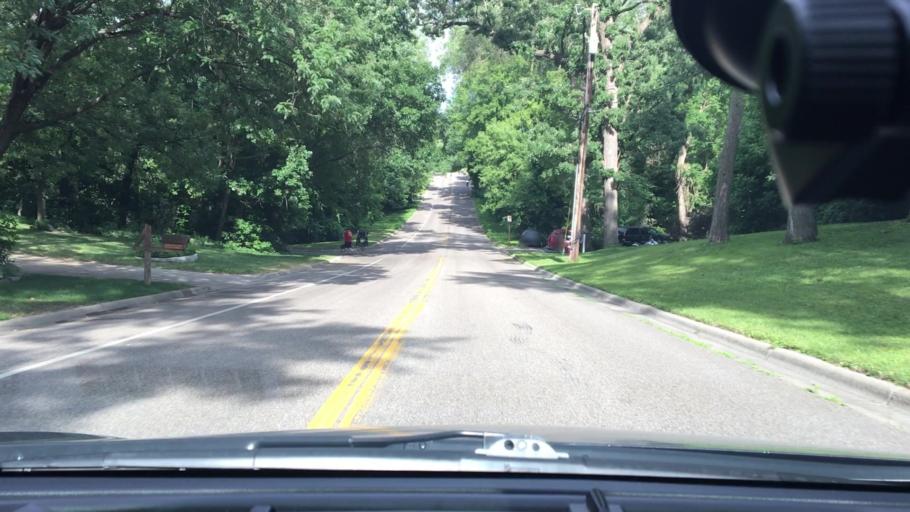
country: US
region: Minnesota
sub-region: Hennepin County
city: Plymouth
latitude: 45.0073
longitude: -93.4368
